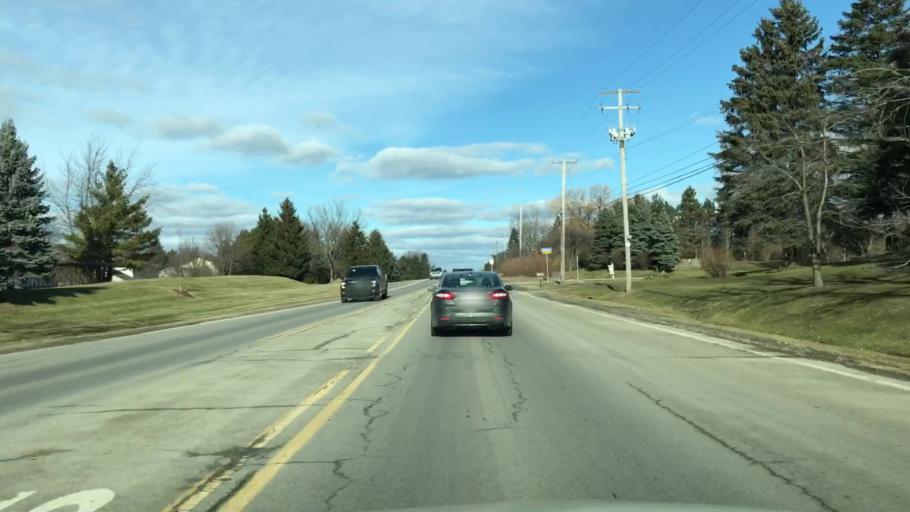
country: US
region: Michigan
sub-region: Oakland County
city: Auburn Hills
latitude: 42.6873
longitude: -83.1943
